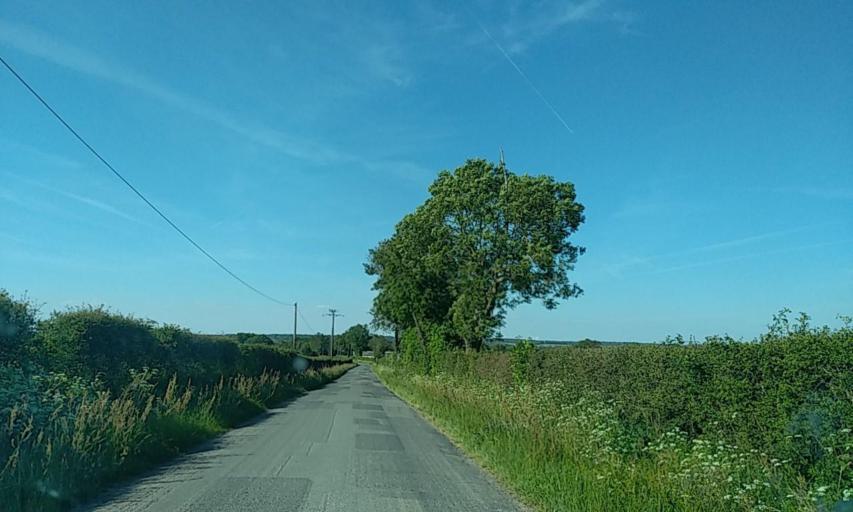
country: FR
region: Poitou-Charentes
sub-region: Departement des Deux-Sevres
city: Boisme
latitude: 46.8078
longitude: -0.4155
